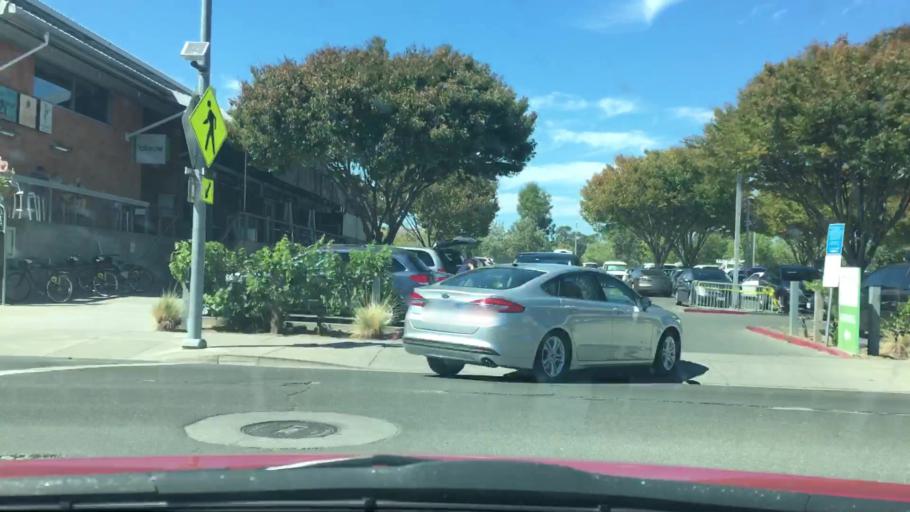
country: US
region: California
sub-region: Napa County
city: Napa
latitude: 38.3014
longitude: -122.2810
